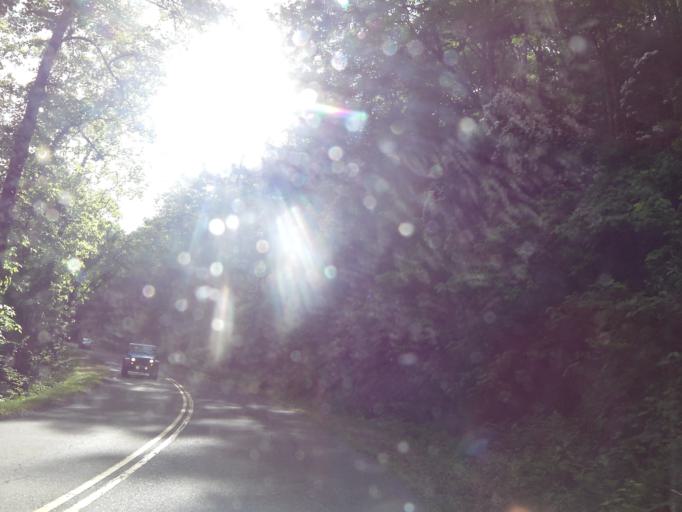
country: US
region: Tennessee
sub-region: Sevier County
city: Gatlinburg
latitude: 35.6634
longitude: -83.6178
